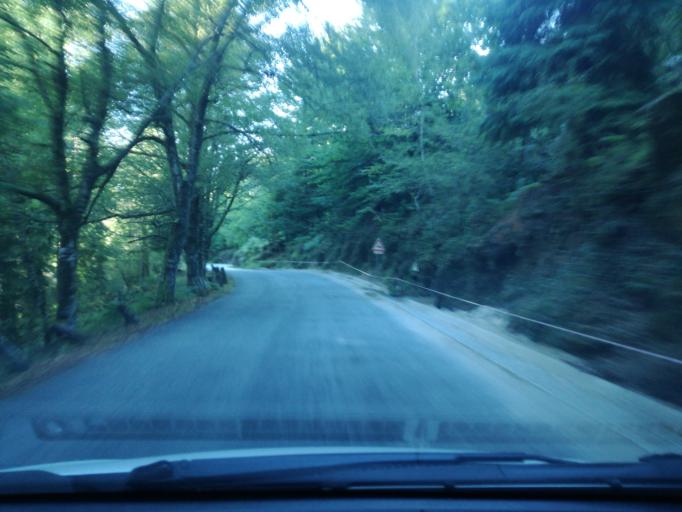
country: ES
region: Galicia
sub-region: Provincia de Ourense
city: Lobios
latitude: 41.7683
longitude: -8.1457
